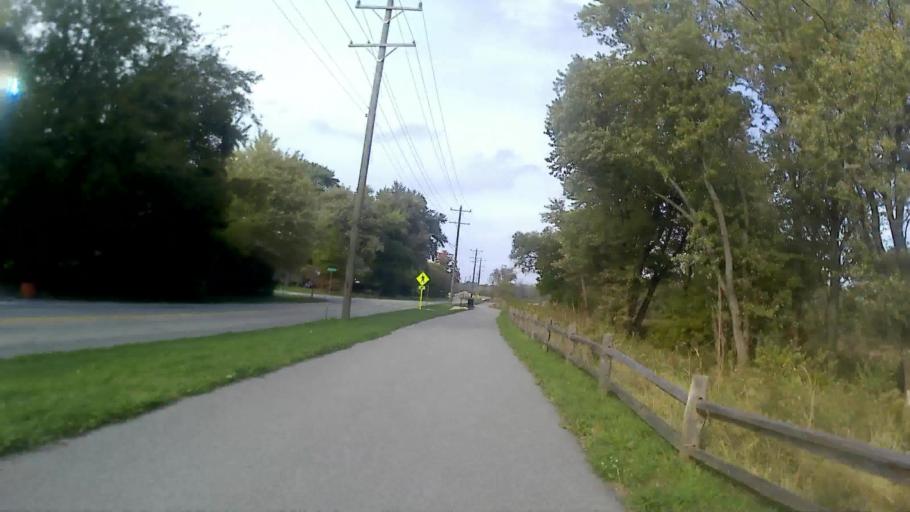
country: US
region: Illinois
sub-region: DuPage County
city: Warrenville
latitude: 41.8123
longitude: -88.1744
